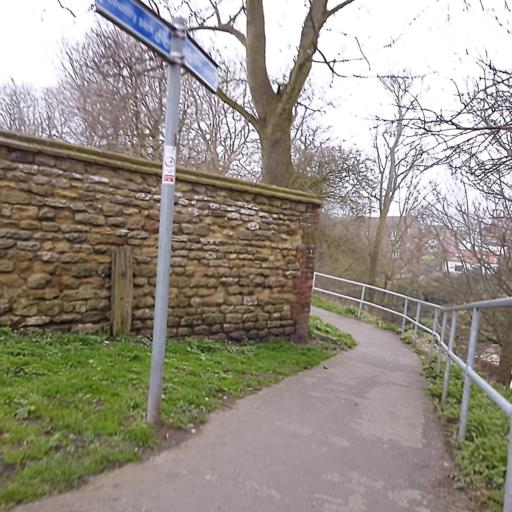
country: GB
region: England
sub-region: North Yorkshire
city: Filey
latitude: 54.2138
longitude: -0.2888
